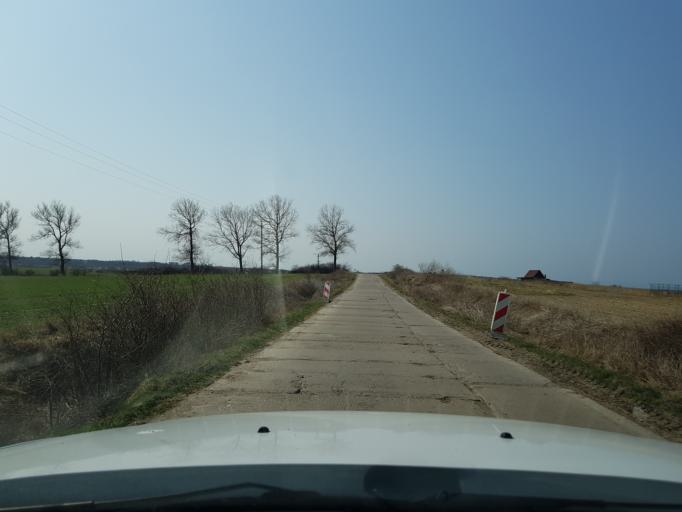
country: PL
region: West Pomeranian Voivodeship
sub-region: Powiat slawienski
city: Darlowo
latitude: 54.4438
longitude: 16.4185
